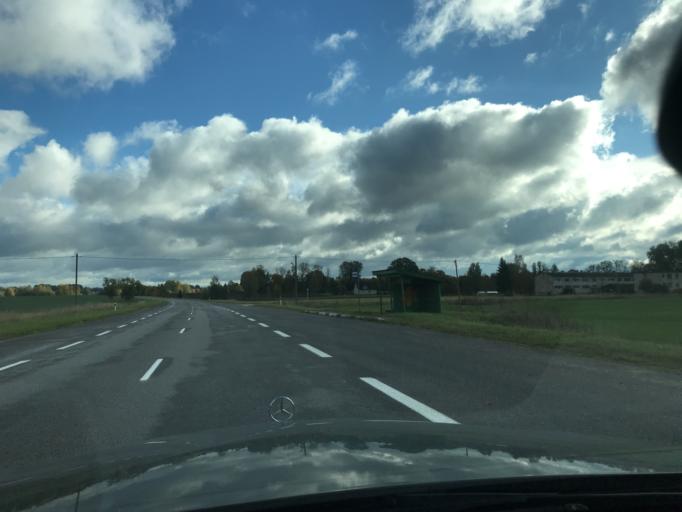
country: EE
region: Valgamaa
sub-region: Torva linn
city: Torva
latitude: 57.9777
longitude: 25.9826
